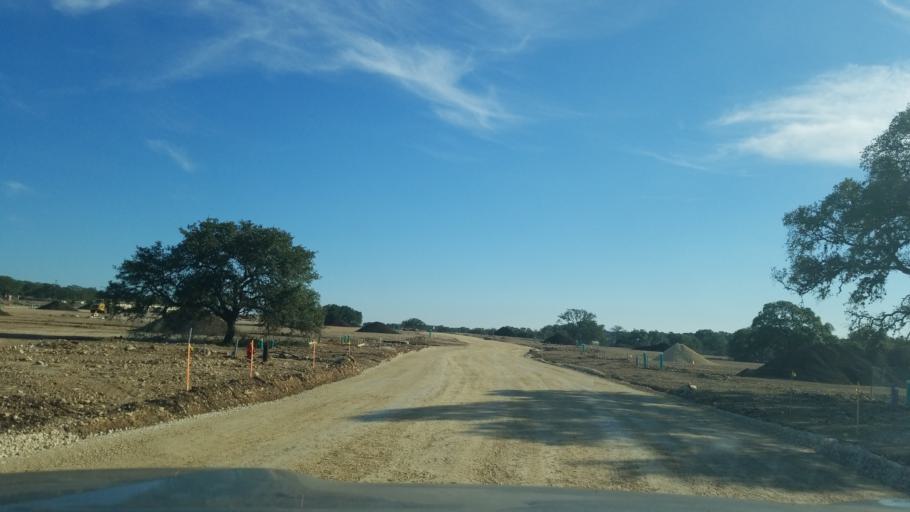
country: US
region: Texas
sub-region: Comal County
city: Canyon Lake
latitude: 29.7892
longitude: -98.2894
